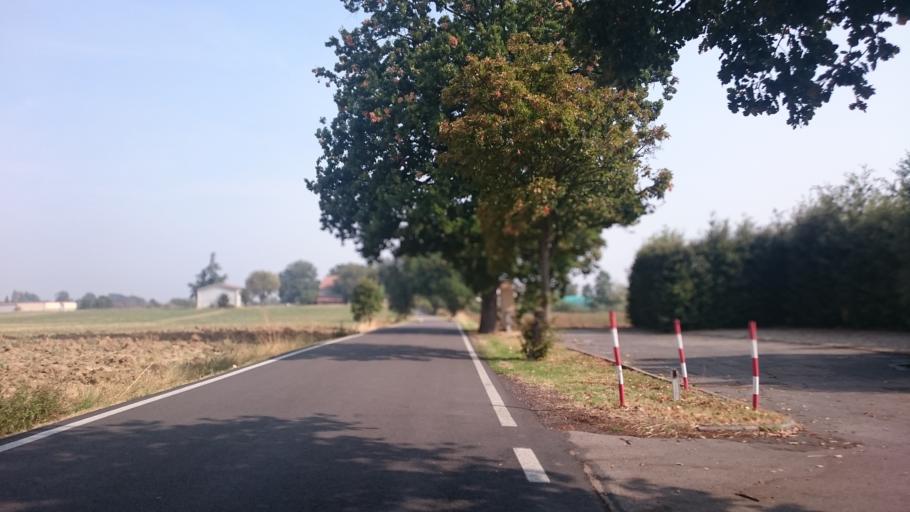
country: IT
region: Emilia-Romagna
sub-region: Provincia di Reggio Emilia
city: Fogliano
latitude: 44.6488
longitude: 10.6239
